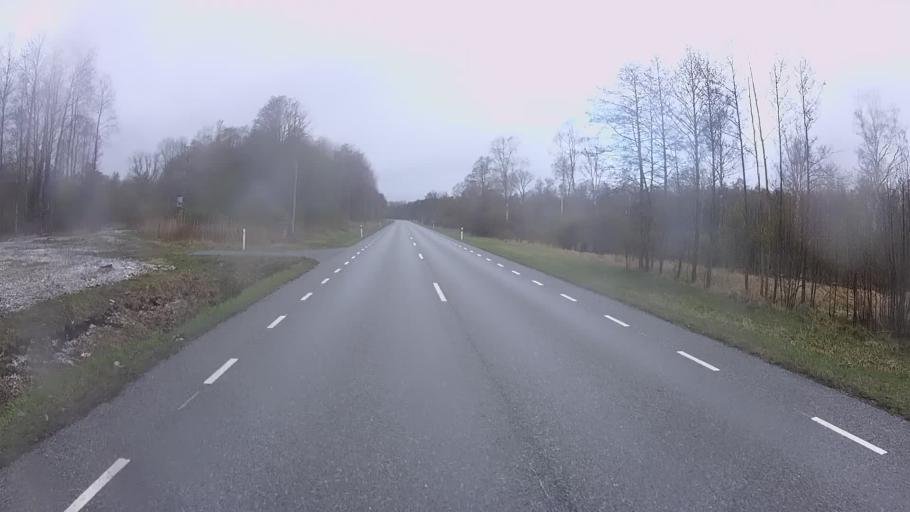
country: EE
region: Hiiumaa
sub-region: Kaerdla linn
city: Kardla
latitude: 59.0027
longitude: 22.5787
